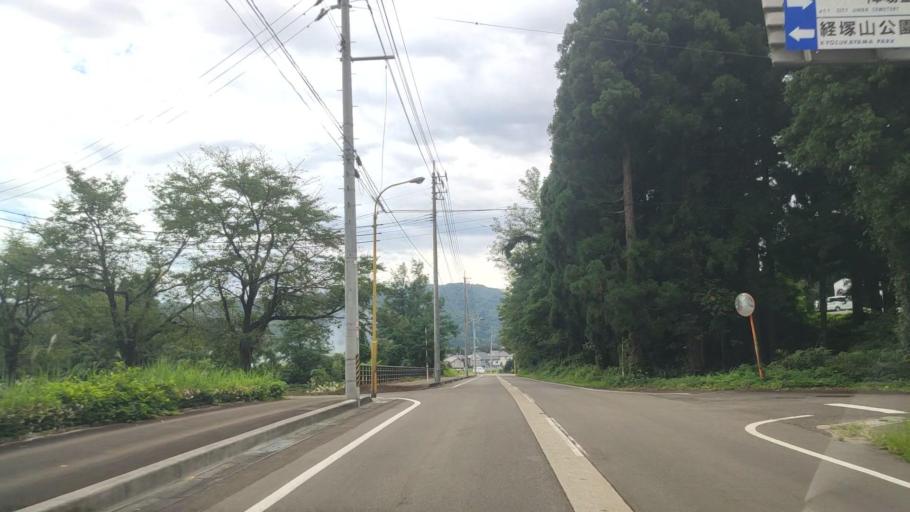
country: JP
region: Niigata
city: Arai
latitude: 37.0126
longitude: 138.2541
